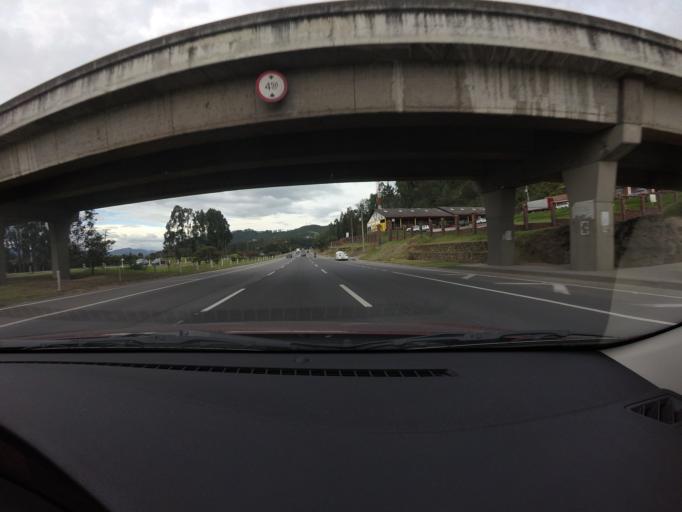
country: CO
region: Cundinamarca
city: Cajica
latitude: 4.9314
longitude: -73.9916
